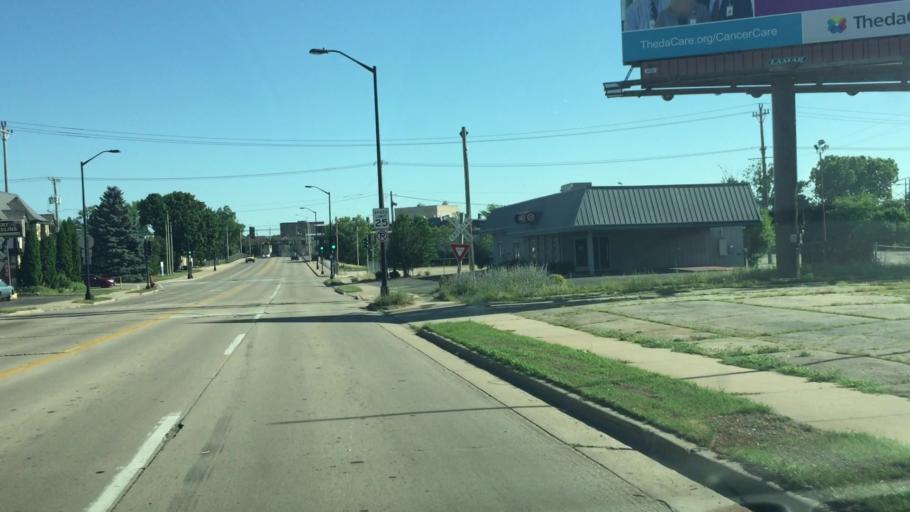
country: US
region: Wisconsin
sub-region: Winnebago County
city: Menasha
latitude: 44.1946
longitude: -88.4541
